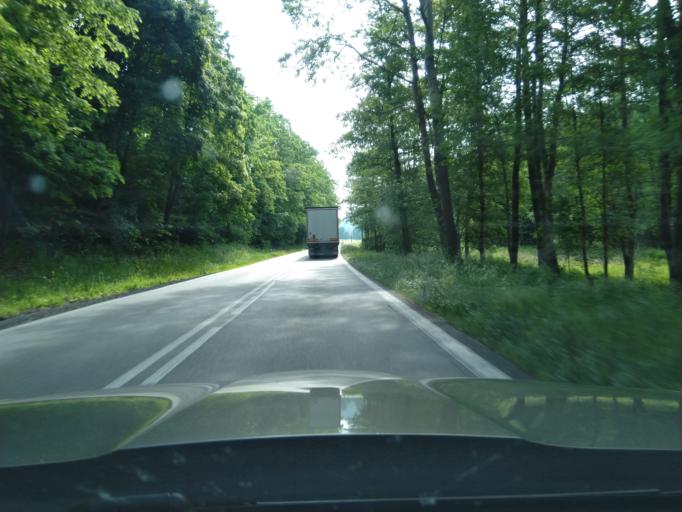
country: CZ
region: Jihocesky
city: Lhenice
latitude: 49.0523
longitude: 14.1324
